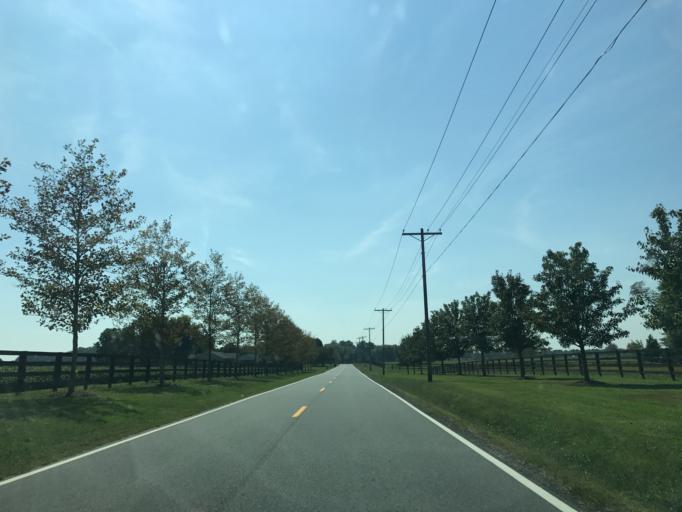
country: US
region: Delaware
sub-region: New Castle County
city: Middletown
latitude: 39.5011
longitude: -75.8051
